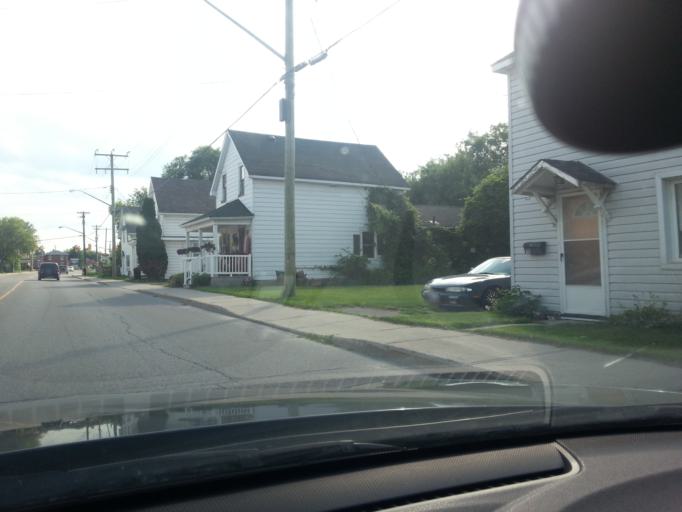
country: CA
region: Ontario
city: Arnprior
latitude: 45.4279
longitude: -76.3605
